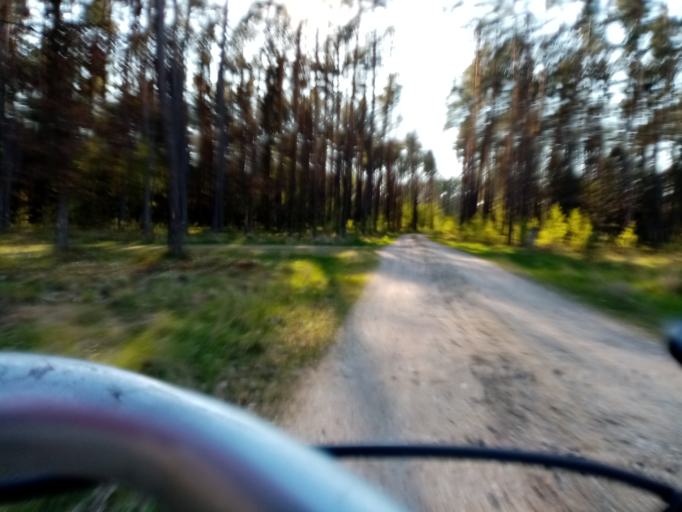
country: PL
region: Kujawsko-Pomorskie
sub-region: Powiat brodnicki
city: Gorzno
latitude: 53.1593
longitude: 19.6884
